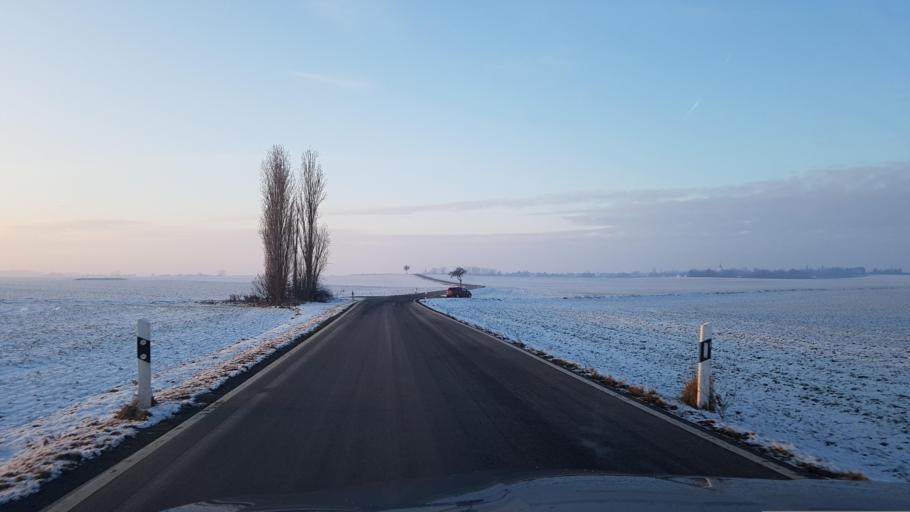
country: DE
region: Saxony
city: Jesewitz
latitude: 51.4225
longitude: 12.5308
